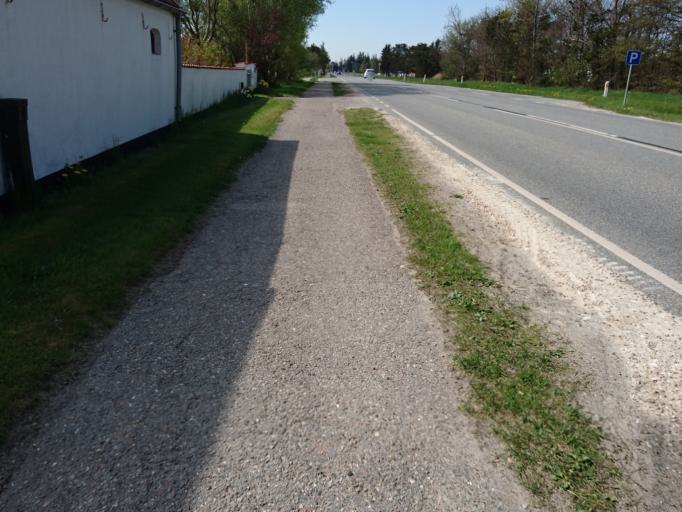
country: DK
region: North Denmark
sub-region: Frederikshavn Kommune
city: Strandby
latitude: 57.6036
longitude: 10.4222
